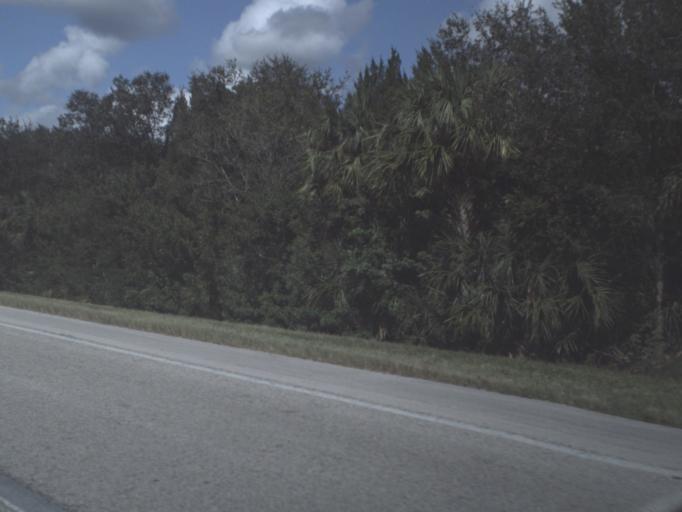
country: US
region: Florida
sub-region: Brevard County
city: Port Saint John
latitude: 28.4530
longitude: -80.8786
